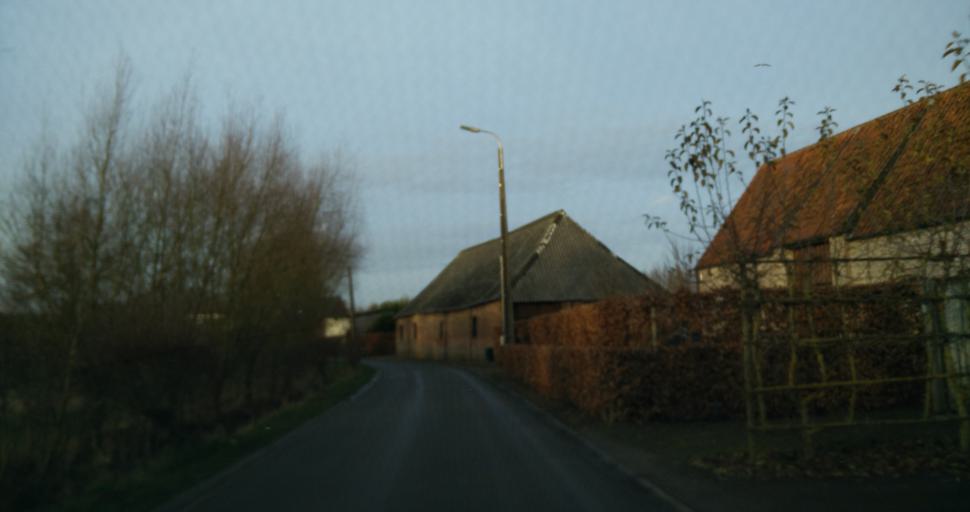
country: BE
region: Flanders
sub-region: Provincie Oost-Vlaanderen
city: Temse
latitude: 51.1072
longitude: 4.2216
